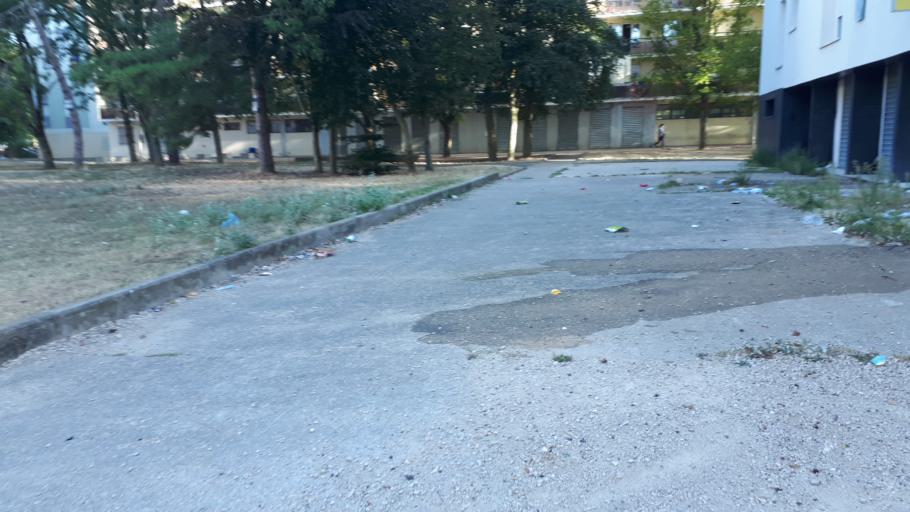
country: FR
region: Centre
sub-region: Departement du Loir-et-Cher
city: Blois
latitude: 47.5901
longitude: 1.3041
